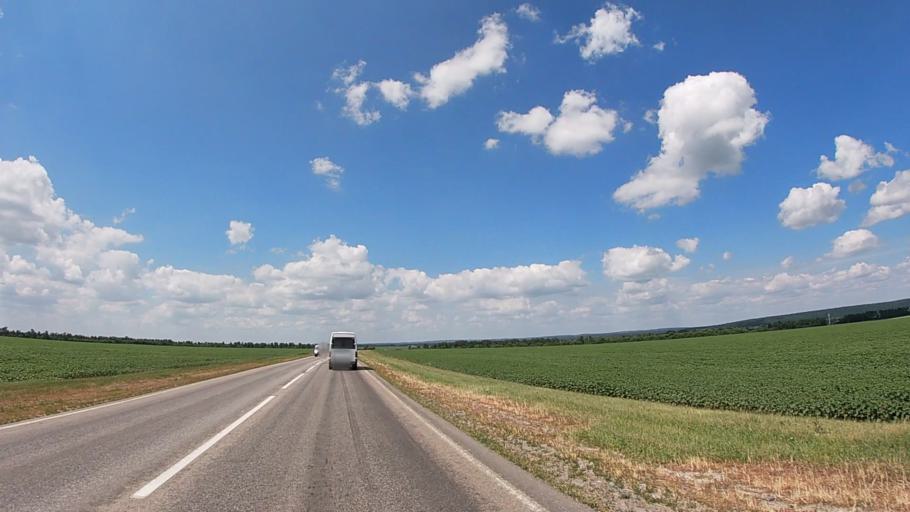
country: RU
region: Belgorod
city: Borisovka
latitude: 50.5751
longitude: 36.0156
